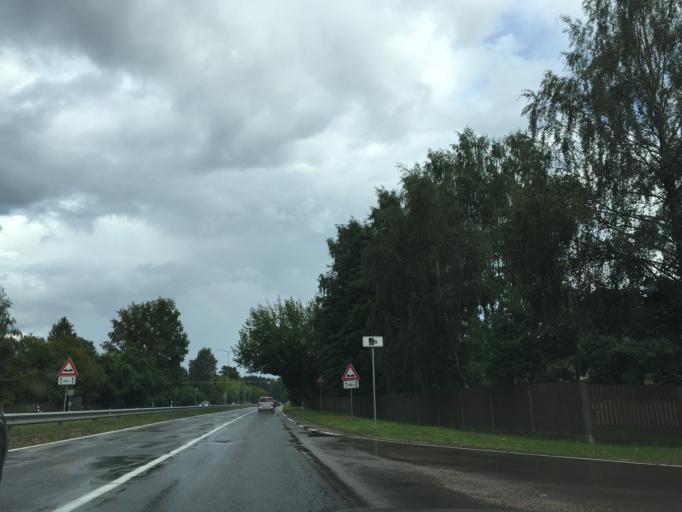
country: LV
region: Babite
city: Pinki
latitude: 56.9599
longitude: 23.9514
